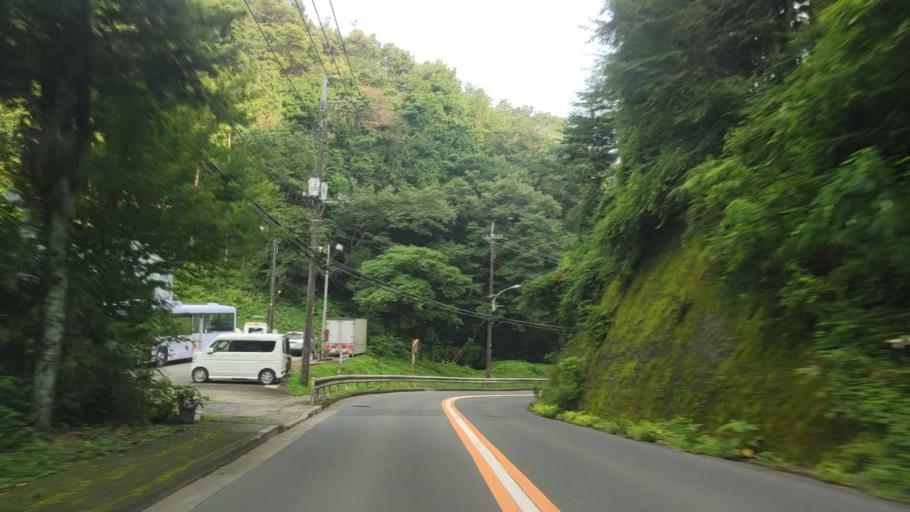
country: JP
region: Saitama
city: Hanno
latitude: 35.8252
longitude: 139.2744
